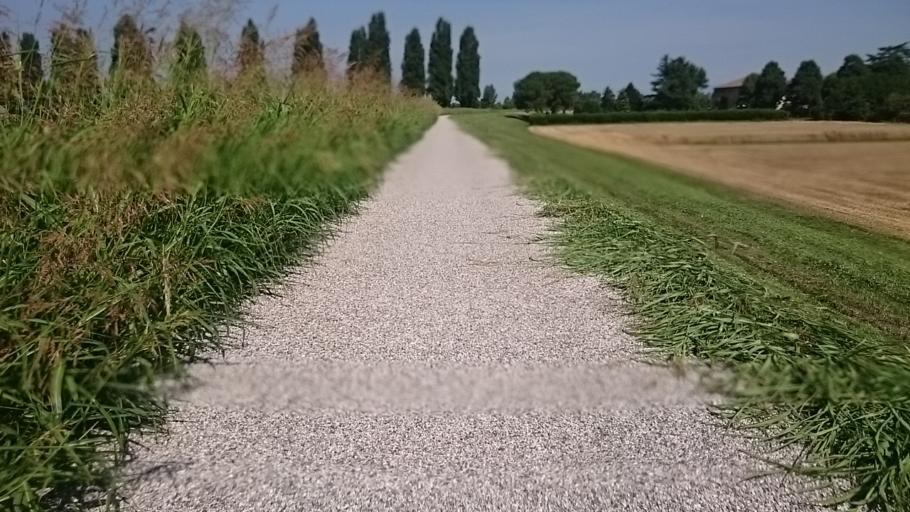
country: IT
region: Veneto
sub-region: Provincia di Padova
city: Saccolongo
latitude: 45.4089
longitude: 11.7505
